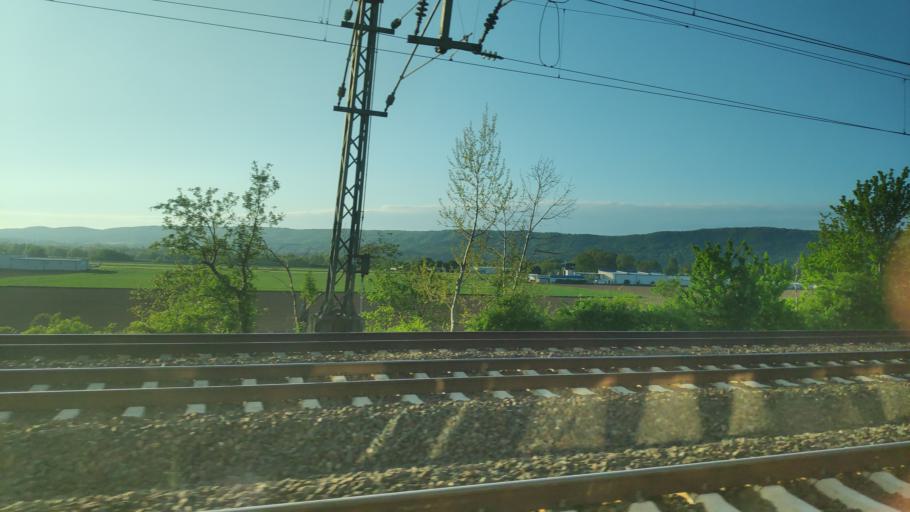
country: DE
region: North Rhine-Westphalia
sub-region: Regierungsbezirk Detmold
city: Vlotho
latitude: 52.2179
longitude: 8.8649
